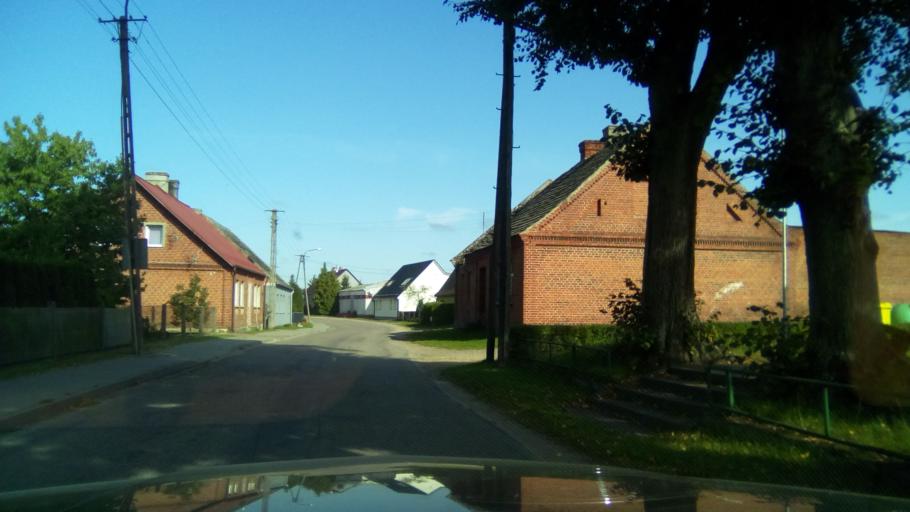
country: PL
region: Greater Poland Voivodeship
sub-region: Powiat zlotowski
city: Sypniewo
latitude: 53.3488
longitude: 16.5732
